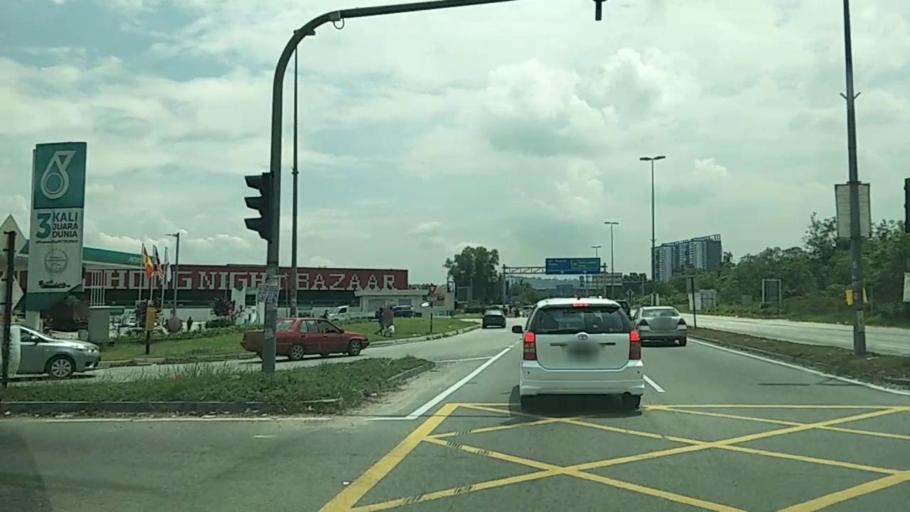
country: MY
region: Selangor
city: Subang Jaya
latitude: 2.9784
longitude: 101.6130
